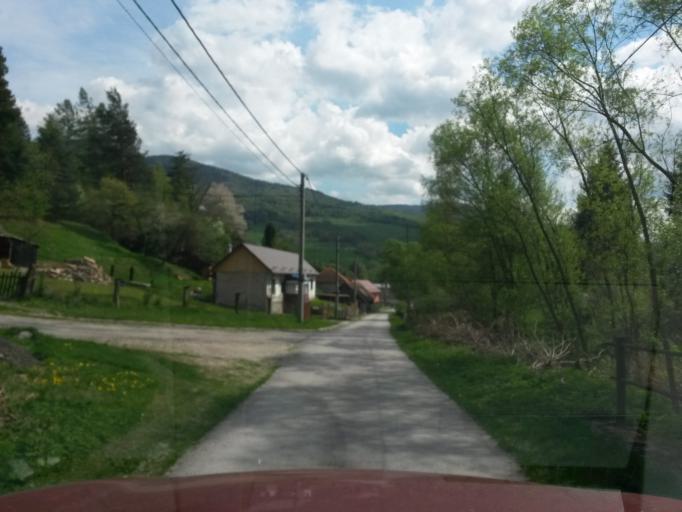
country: SK
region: Kosicky
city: Krompachy
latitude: 48.8111
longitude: 20.8082
